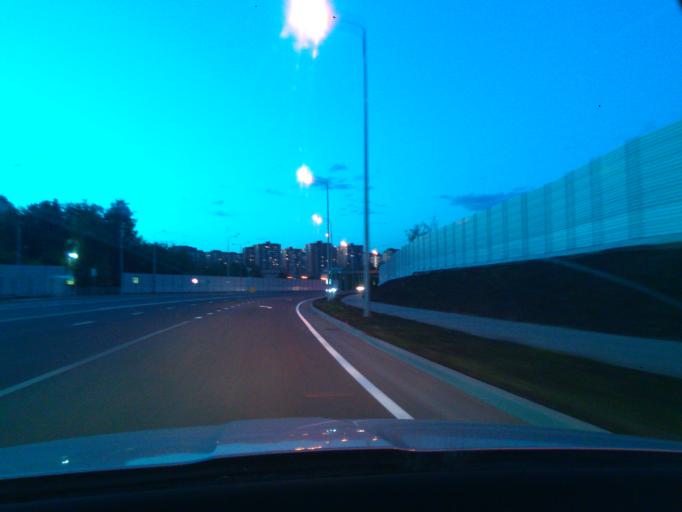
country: RU
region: Moskovskaya
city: Dolgoprudnyy
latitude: 55.9547
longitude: 37.5169
